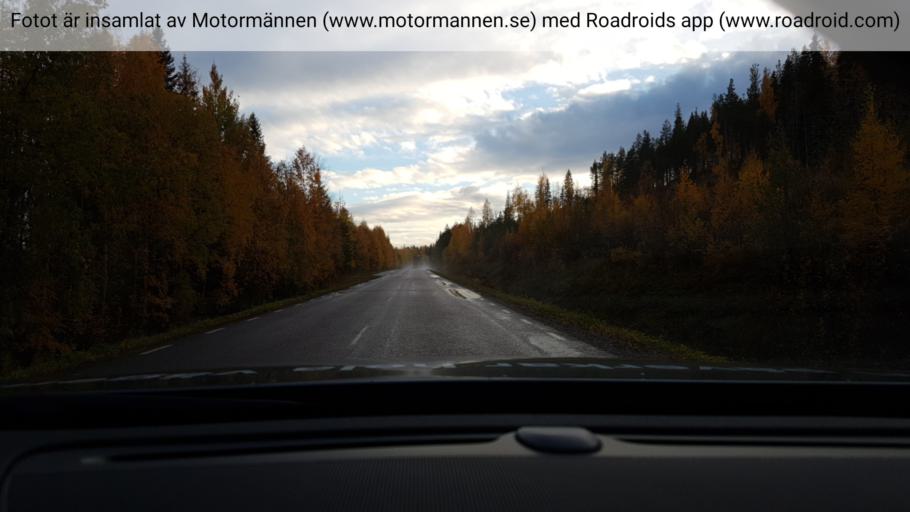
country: SE
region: Norrbotten
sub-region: Overkalix Kommun
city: OEverkalix
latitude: 66.7962
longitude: 22.7270
